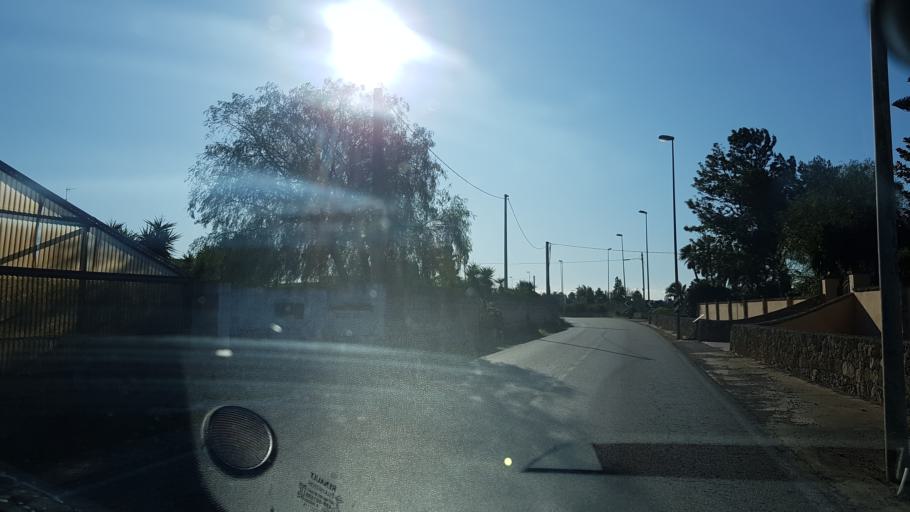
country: IT
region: Apulia
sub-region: Provincia di Lecce
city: Taviano
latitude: 39.9927
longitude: 18.0984
